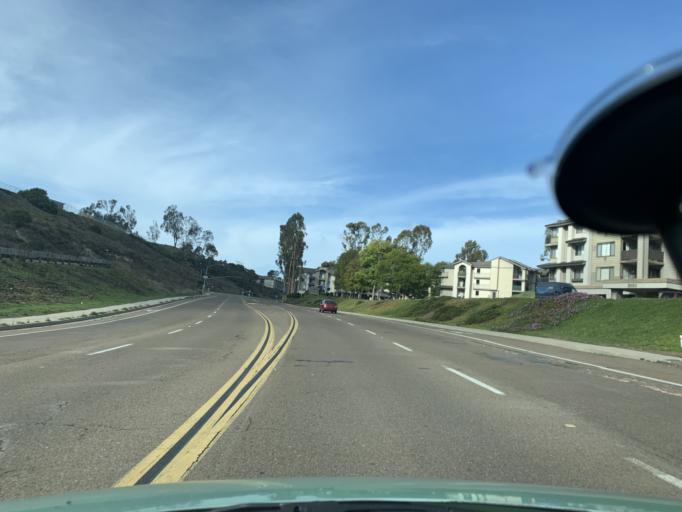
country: US
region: California
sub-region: San Diego County
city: San Diego
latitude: 32.8093
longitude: -117.1767
